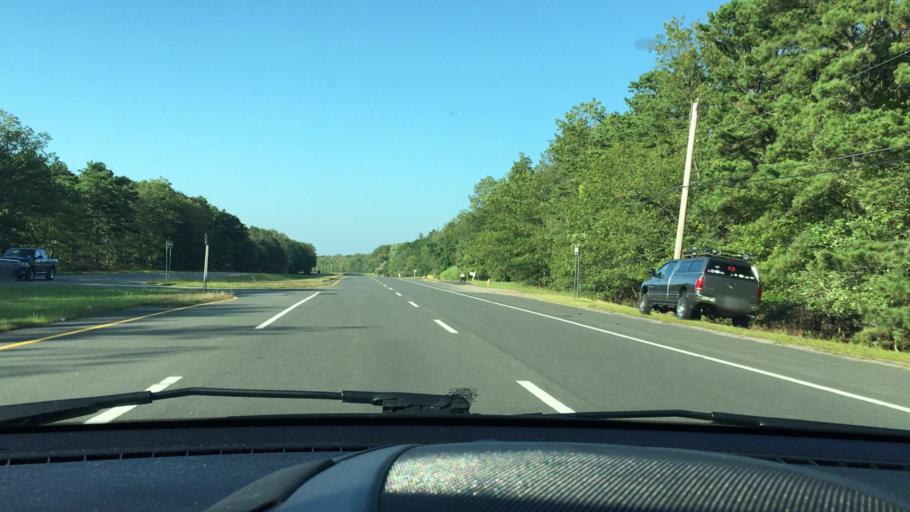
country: US
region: New York
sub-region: Suffolk County
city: Ridge
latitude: 40.9045
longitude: -72.8818
